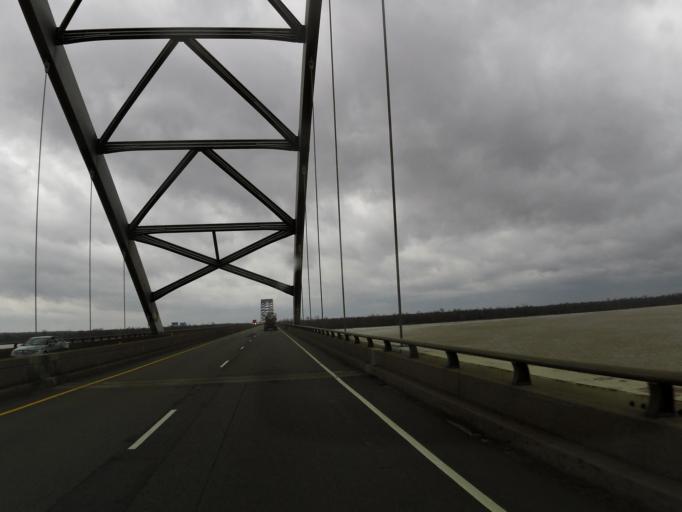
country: US
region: Illinois
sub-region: Massac County
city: Metropolis
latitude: 37.1376
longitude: -88.6857
